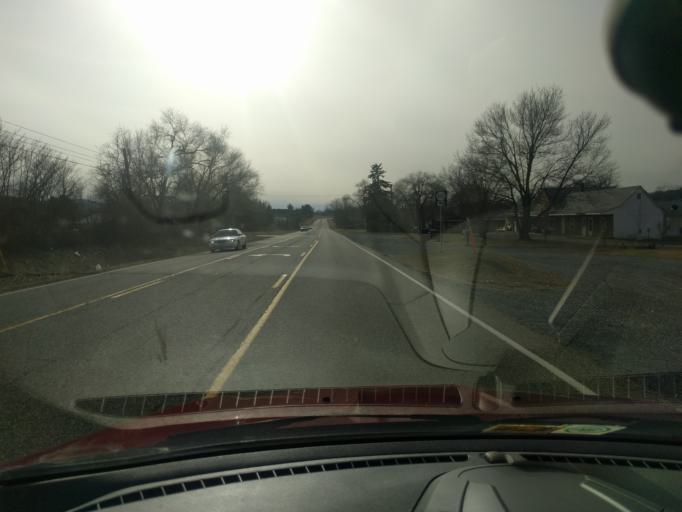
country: US
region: Virginia
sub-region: Augusta County
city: Stuarts Draft
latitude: 37.9838
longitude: -79.1664
